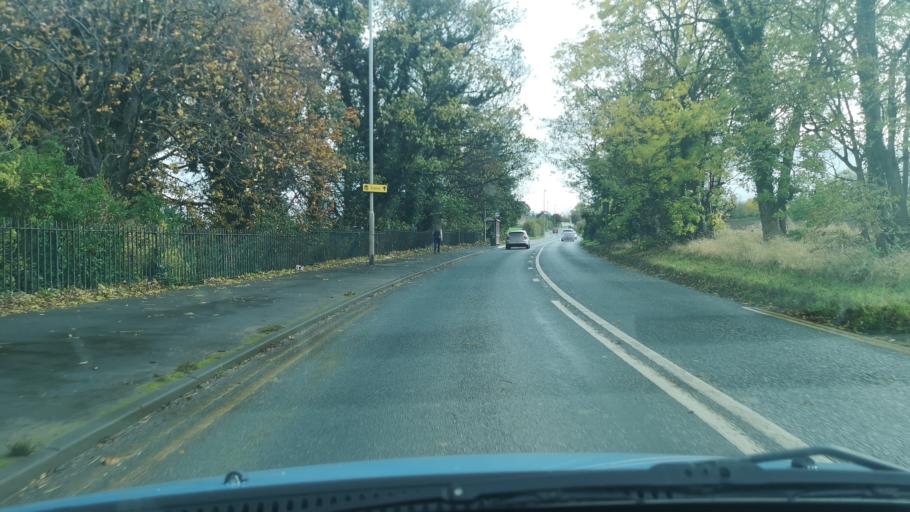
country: GB
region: England
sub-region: City and Borough of Wakefield
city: Hemsworth
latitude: 53.6200
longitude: -1.3603
